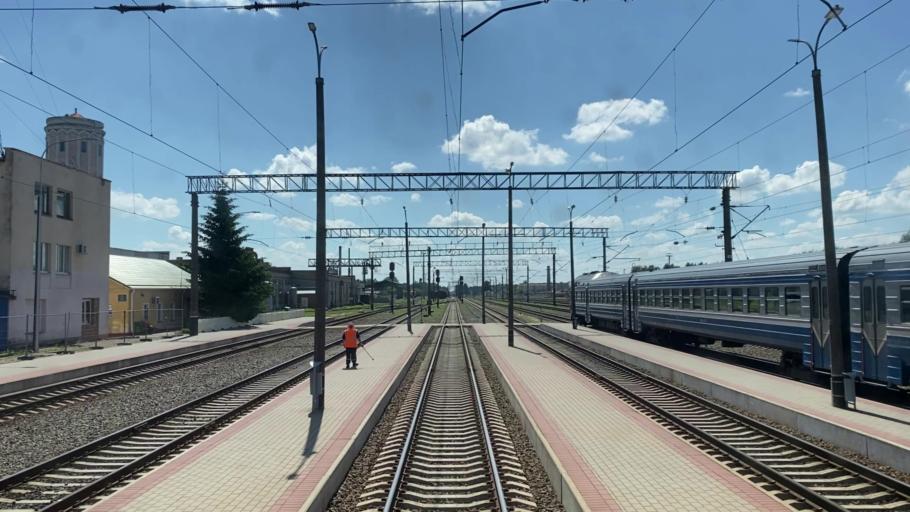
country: BY
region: Brest
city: Baranovichi
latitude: 53.1285
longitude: 26.0430
